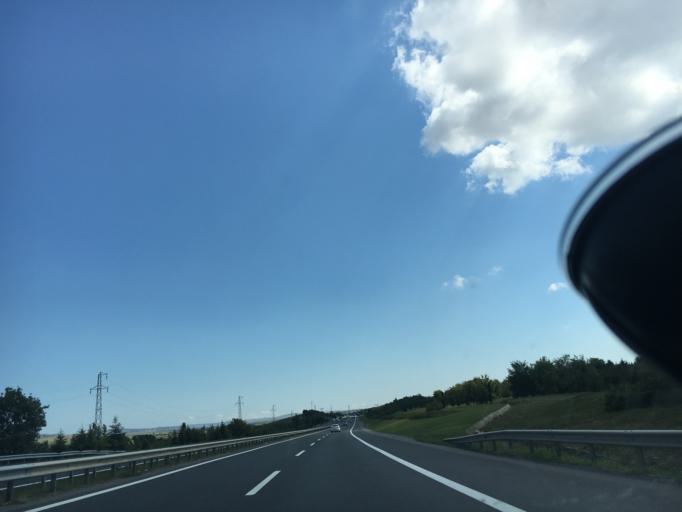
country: TR
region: Istanbul
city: Canta
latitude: 41.0783
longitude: 28.1262
